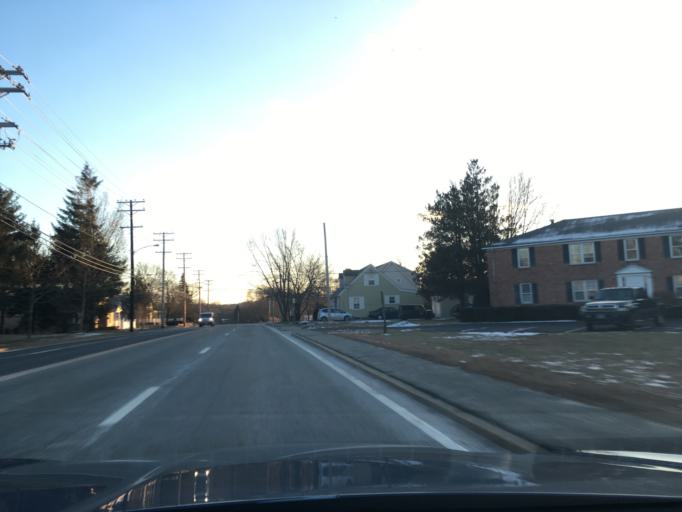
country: US
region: Rhode Island
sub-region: Kent County
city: Warwick
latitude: 41.7131
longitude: -71.4640
